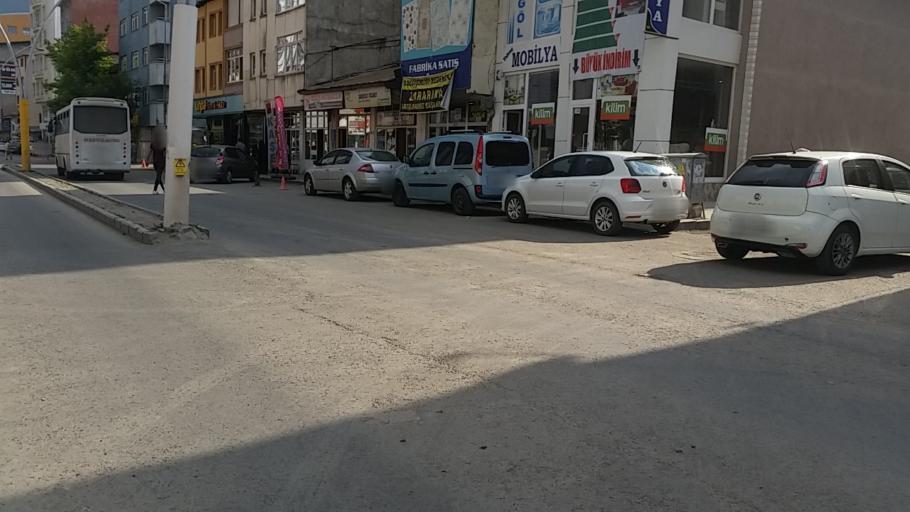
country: TR
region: Agri
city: Agri
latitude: 39.7229
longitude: 43.0510
